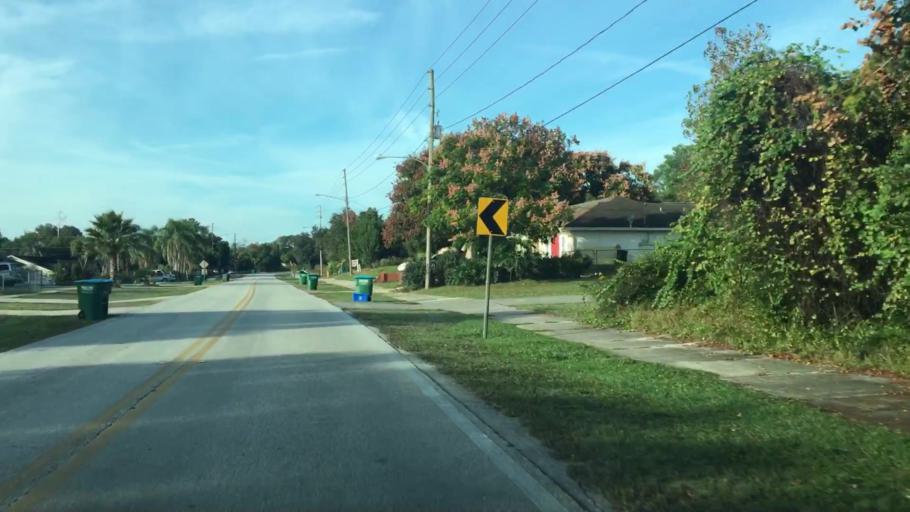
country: US
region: Florida
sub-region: Volusia County
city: Deltona
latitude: 28.9180
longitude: -81.2257
